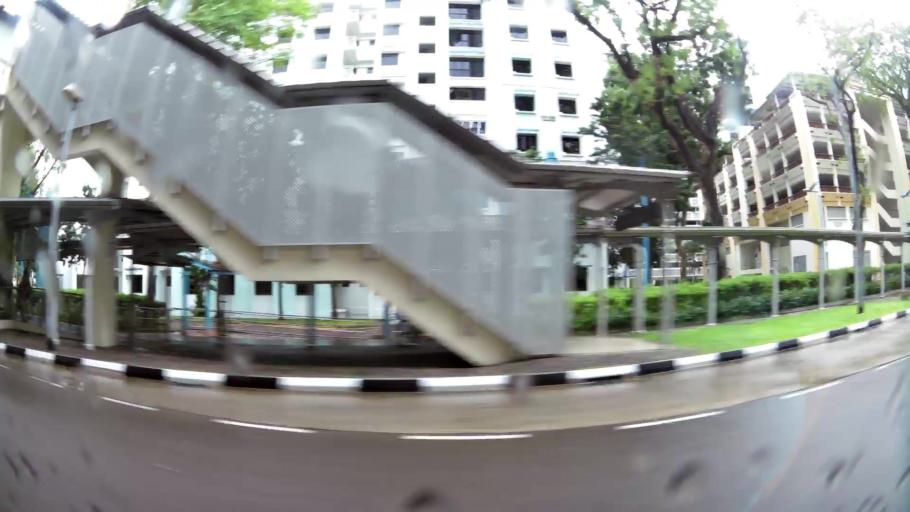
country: MY
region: Johor
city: Kampung Pasir Gudang Baru
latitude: 1.3879
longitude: 103.9056
